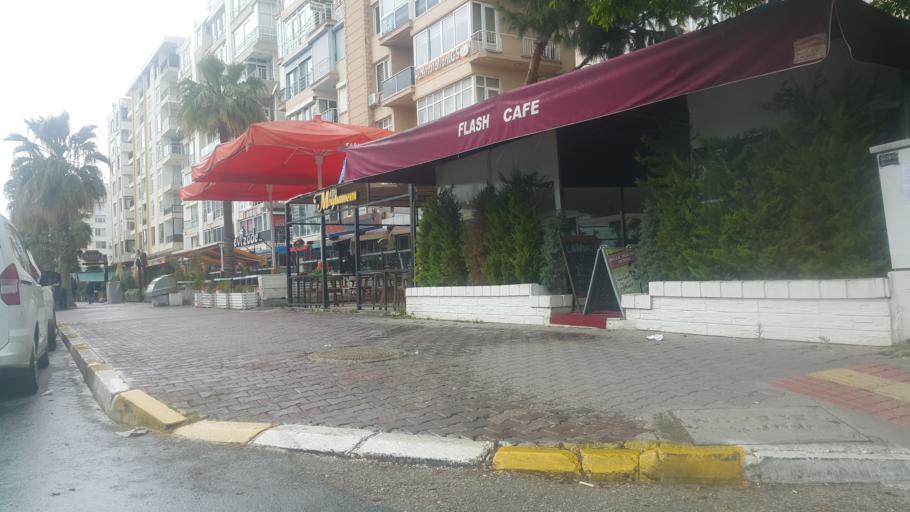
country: TR
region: Mersin
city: Mercin
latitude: 36.7794
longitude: 34.5923
